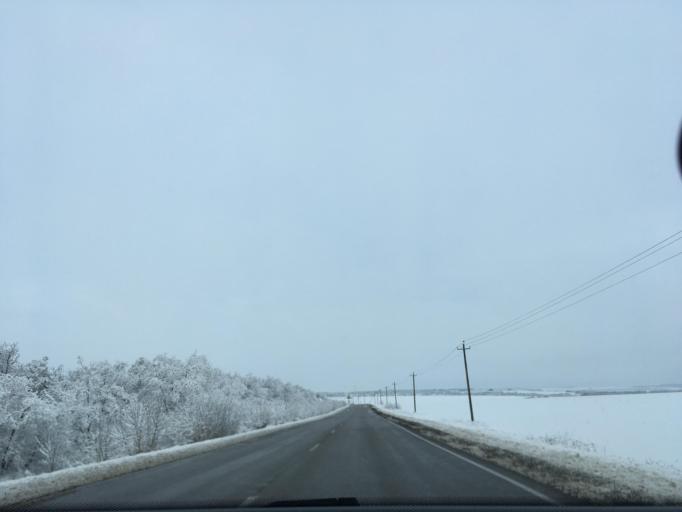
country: RU
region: Voronezj
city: Ol'khovatka
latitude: 50.0198
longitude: 39.0608
